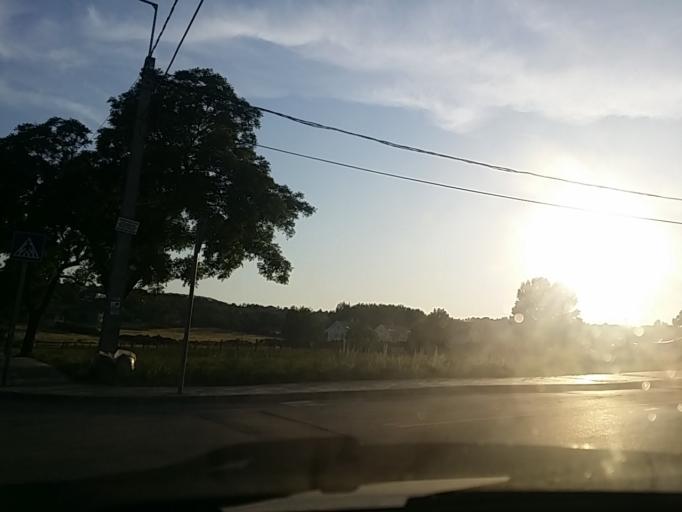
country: HU
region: Pest
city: Urom
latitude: 47.5794
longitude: 19.0347
